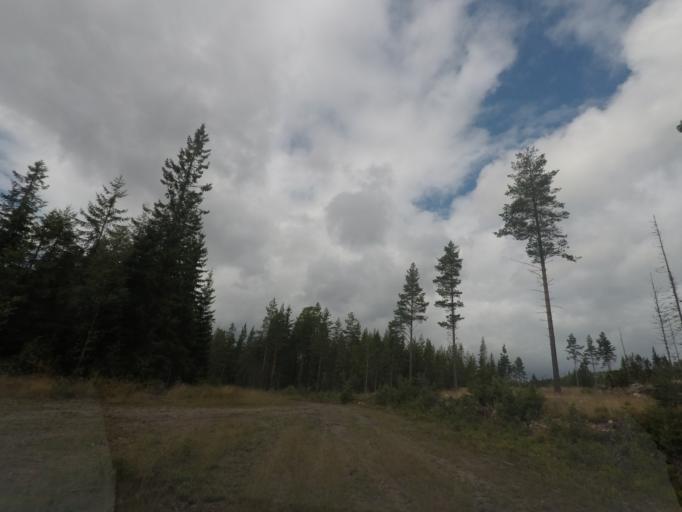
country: SE
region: Vaermland
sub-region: Filipstads Kommun
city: Lesjofors
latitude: 60.1056
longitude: 14.3944
